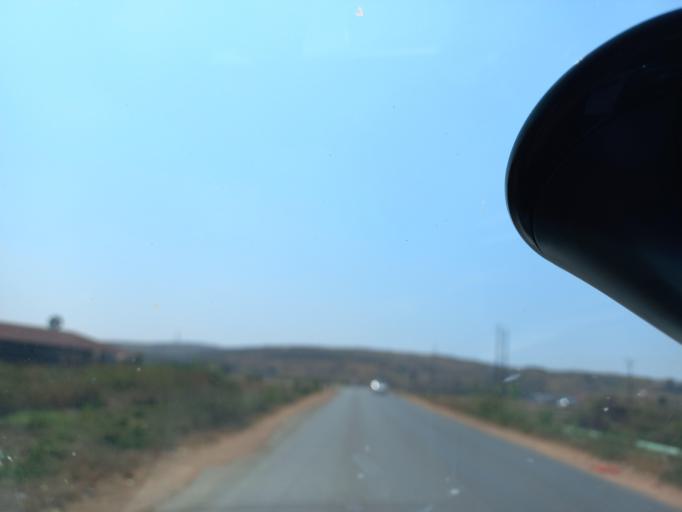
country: ZM
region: Lusaka
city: Kafue
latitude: -15.7591
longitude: 28.1775
